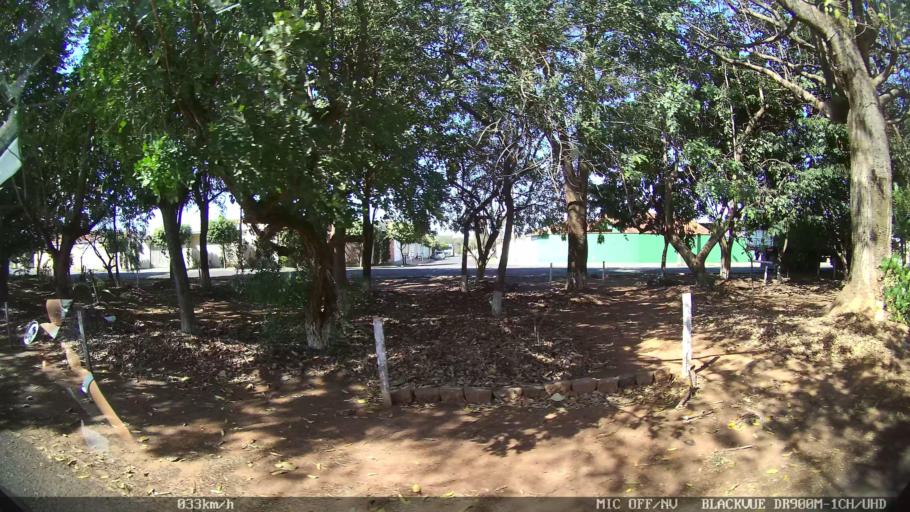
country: BR
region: Sao Paulo
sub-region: Batatais
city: Batatais
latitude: -20.8763
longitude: -47.5950
